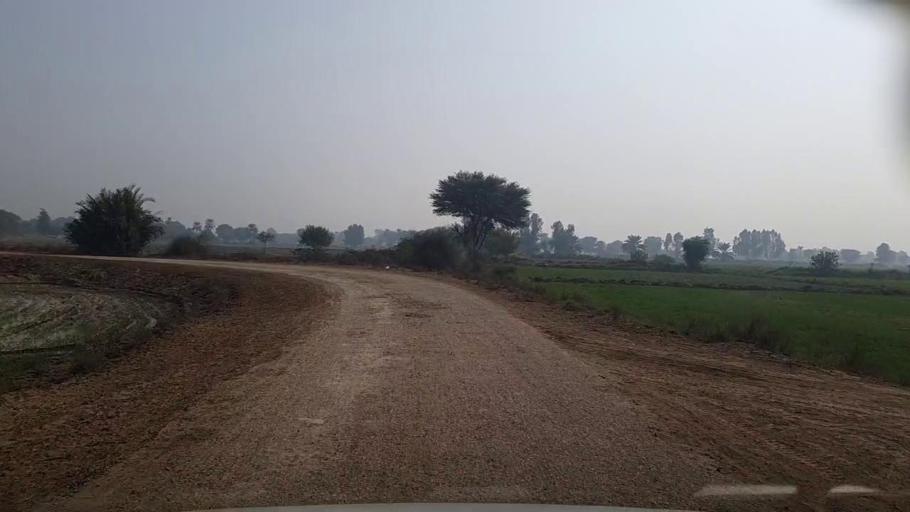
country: PK
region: Sindh
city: Setharja Old
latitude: 27.1432
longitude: 68.4912
